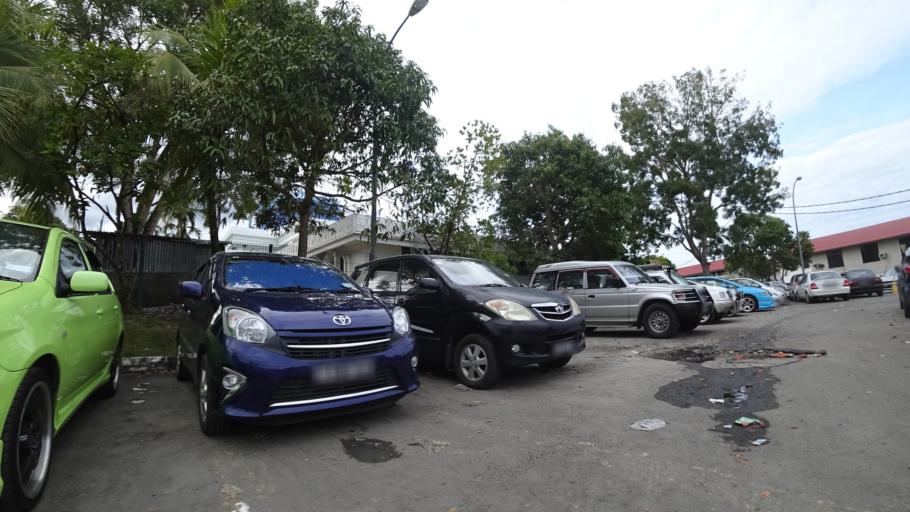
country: BN
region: Brunei and Muara
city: Bandar Seri Begawan
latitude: 4.8524
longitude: 114.9559
